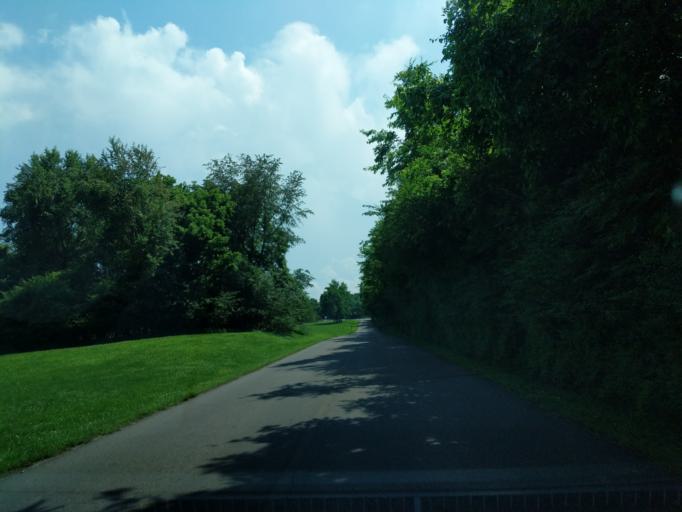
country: US
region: Tennessee
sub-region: Sumner County
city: Hendersonville
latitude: 36.2934
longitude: -86.6610
